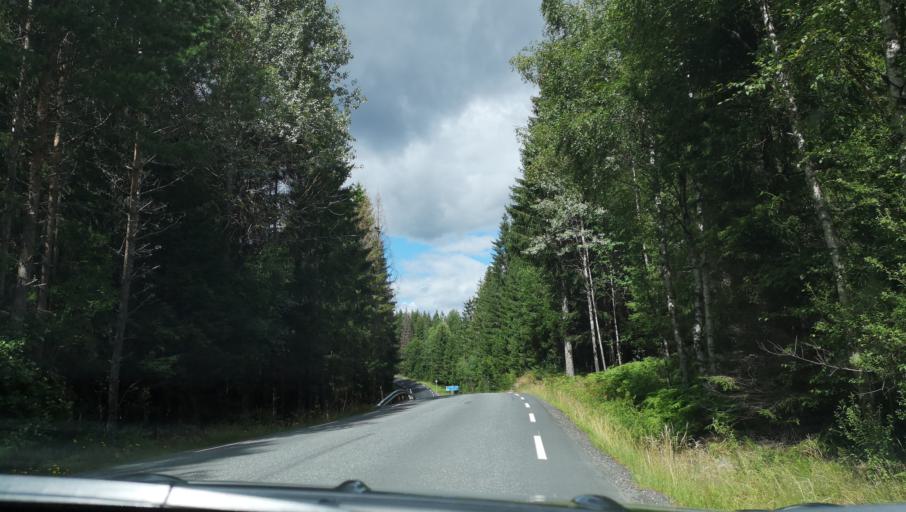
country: NO
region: Ostfold
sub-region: Hobol
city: Tomter
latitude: 59.6777
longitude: 10.9551
